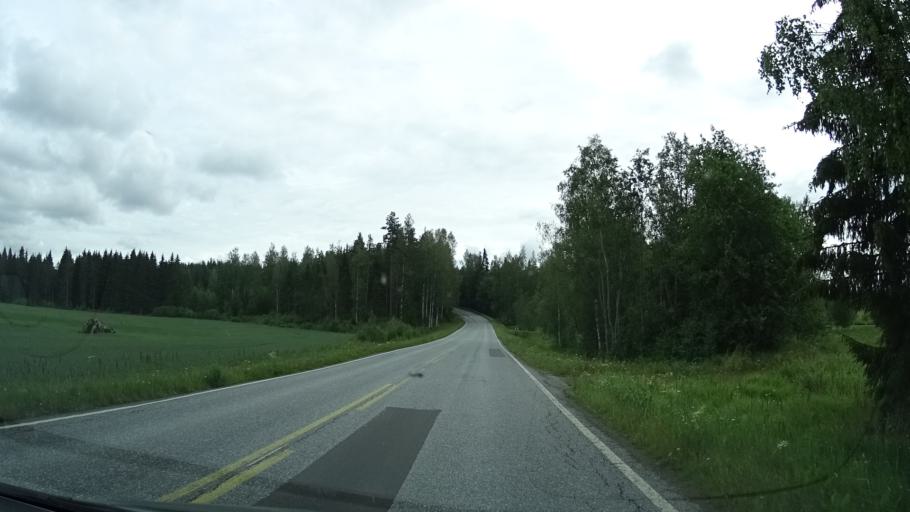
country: FI
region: Pirkanmaa
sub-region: Etelae-Pirkanmaa
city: Urjala
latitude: 61.0893
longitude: 23.5125
